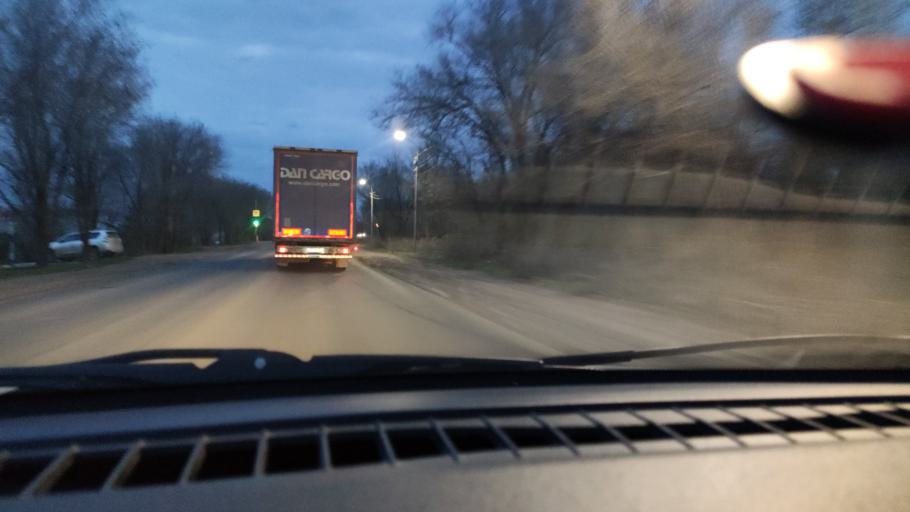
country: RU
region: Orenburg
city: Tatarskaya Kargala
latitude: 51.8766
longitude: 55.1475
